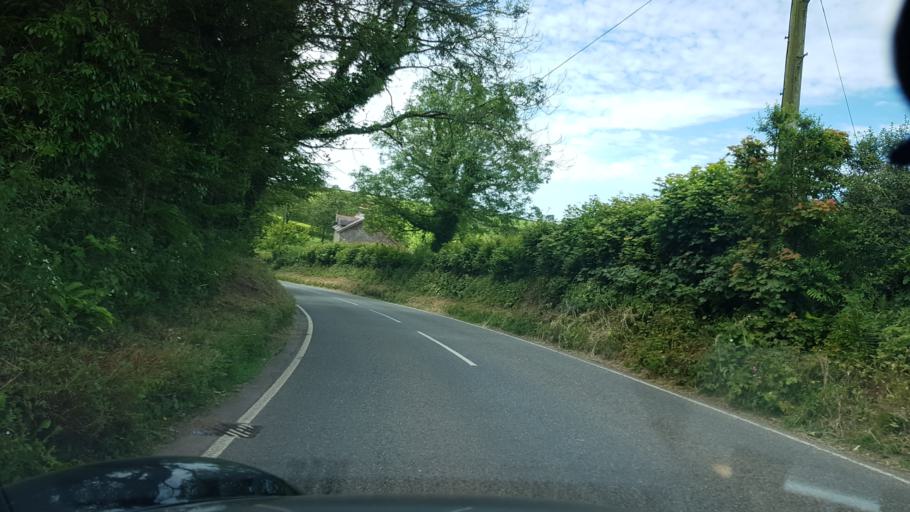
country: GB
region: Wales
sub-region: Carmarthenshire
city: Llanddowror
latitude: 51.7666
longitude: -4.5662
